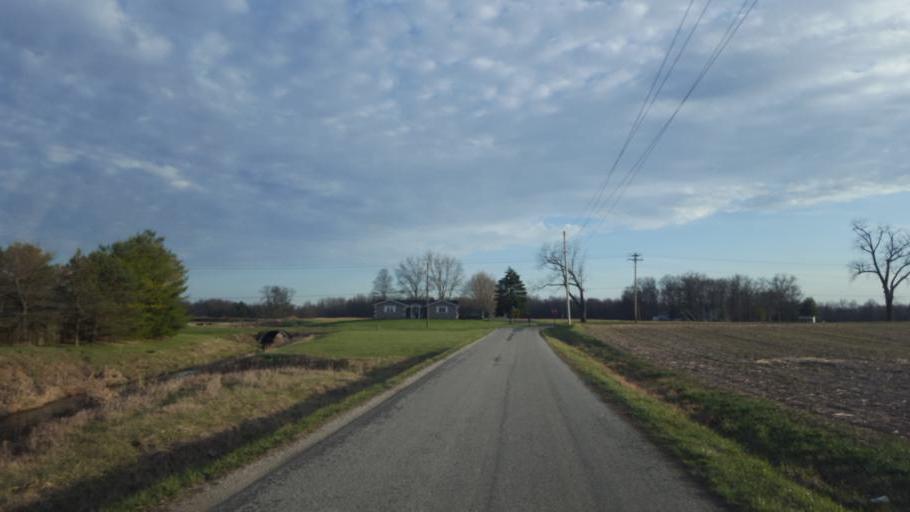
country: US
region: Ohio
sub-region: Marion County
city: Marion
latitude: 40.6026
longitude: -82.9910
